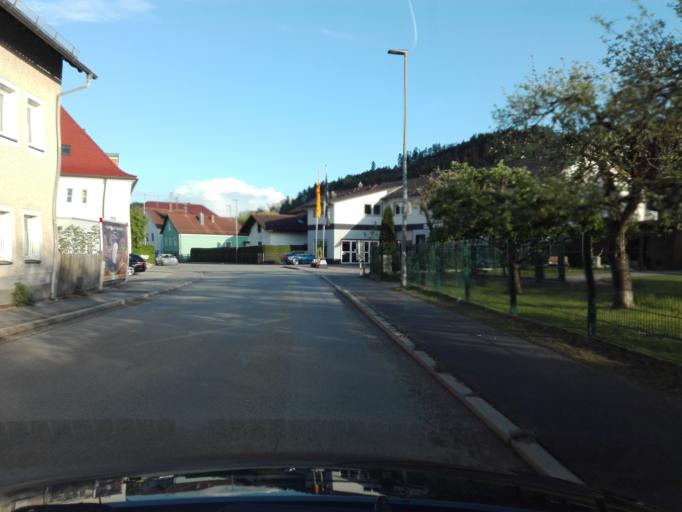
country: DE
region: Bavaria
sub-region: Lower Bavaria
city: Obernzell
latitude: 48.5551
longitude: 13.6334
